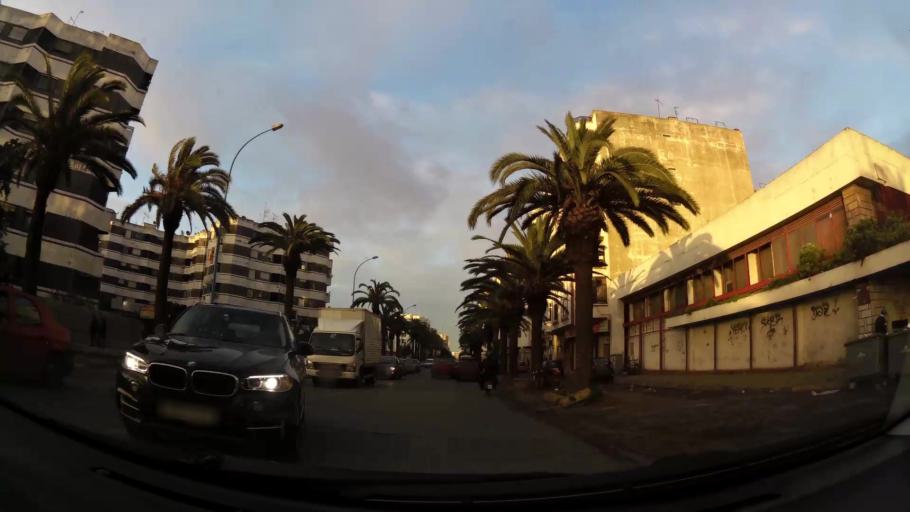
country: MA
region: Grand Casablanca
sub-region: Casablanca
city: Casablanca
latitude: 33.5728
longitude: -7.6464
